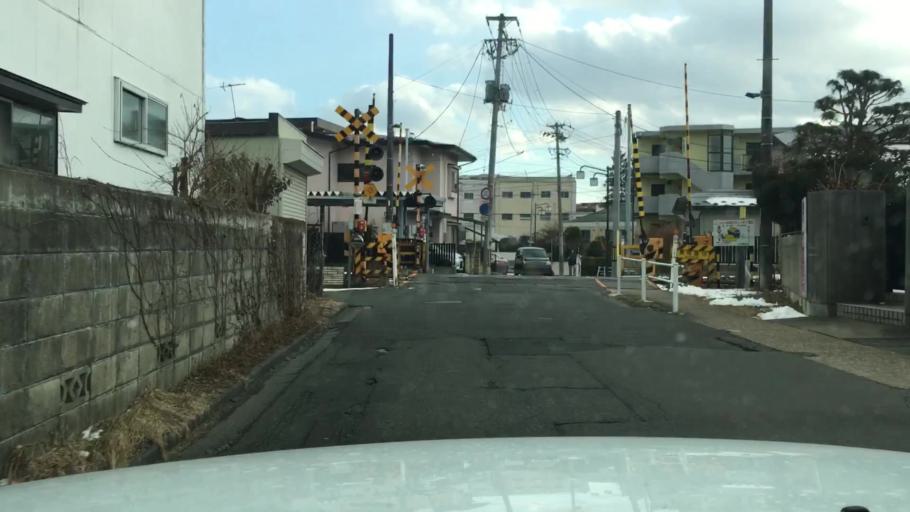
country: JP
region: Iwate
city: Morioka-shi
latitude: 39.7111
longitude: 141.1440
